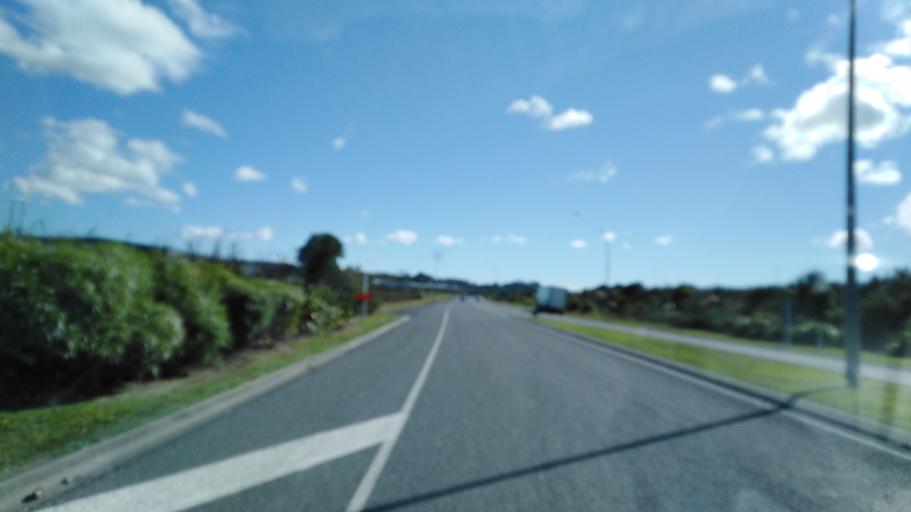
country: NZ
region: Bay of Plenty
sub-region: Tauranga City
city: Tauranga
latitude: -37.7525
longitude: 176.1031
